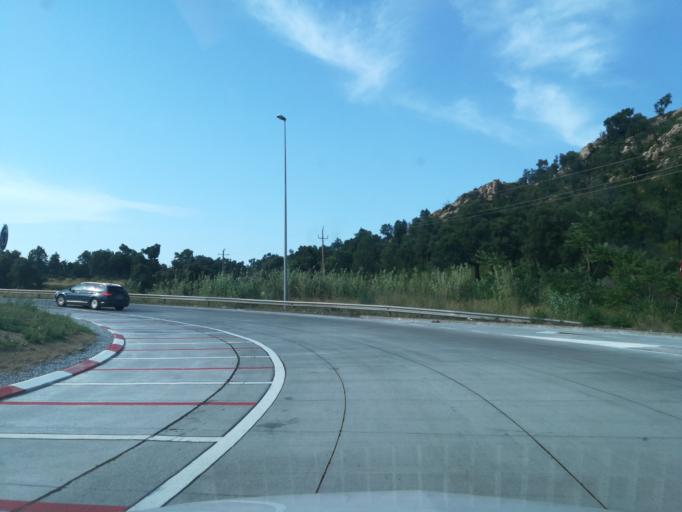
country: ES
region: Catalonia
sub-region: Provincia de Girona
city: la Jonquera
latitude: 42.4334
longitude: 2.8663
